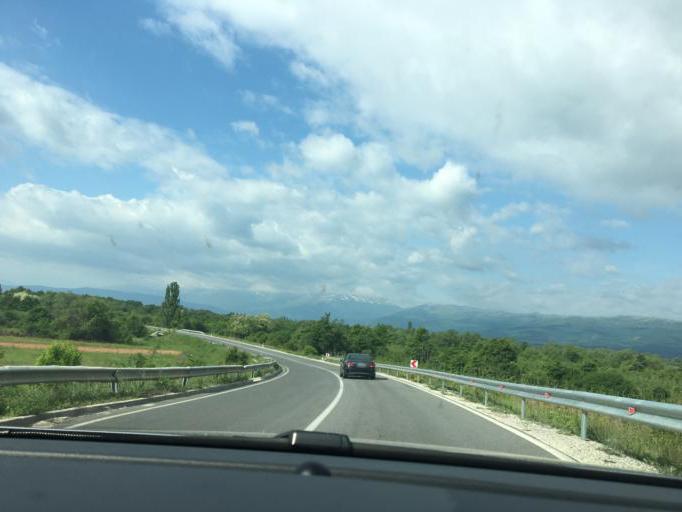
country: MK
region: Resen
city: Resen
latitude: 41.0727
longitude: 21.0558
